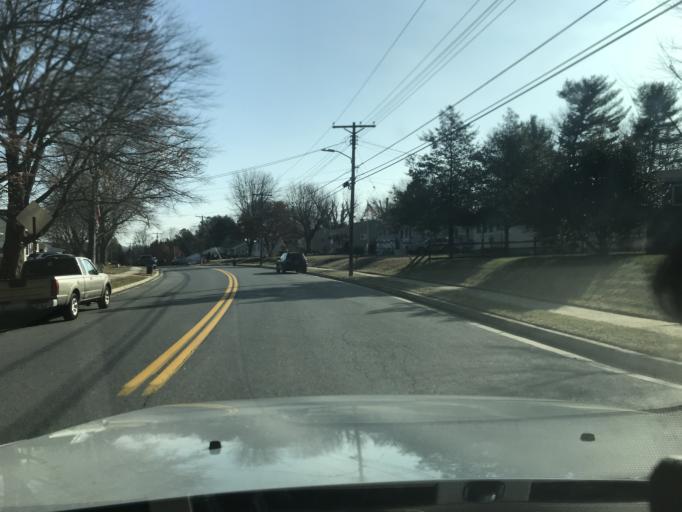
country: US
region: Maryland
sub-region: Baltimore County
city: Owings Mills
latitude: 39.4203
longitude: -76.7944
